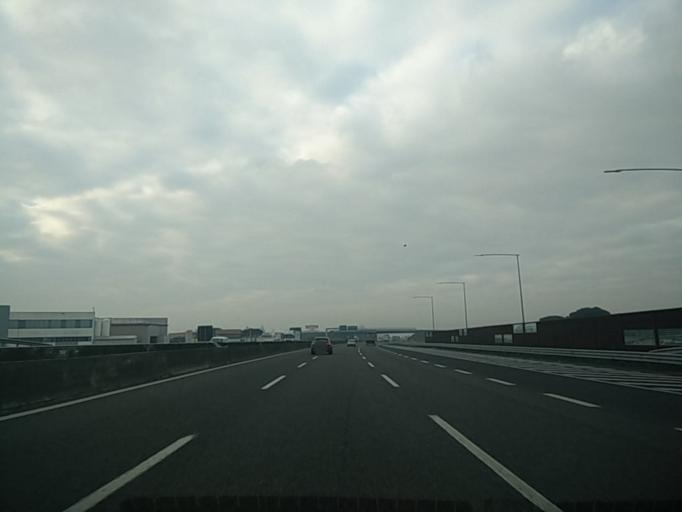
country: IT
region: Emilia-Romagna
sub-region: Forli-Cesena
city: Gatteo-Sant'Angelo
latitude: 44.1217
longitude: 12.3886
